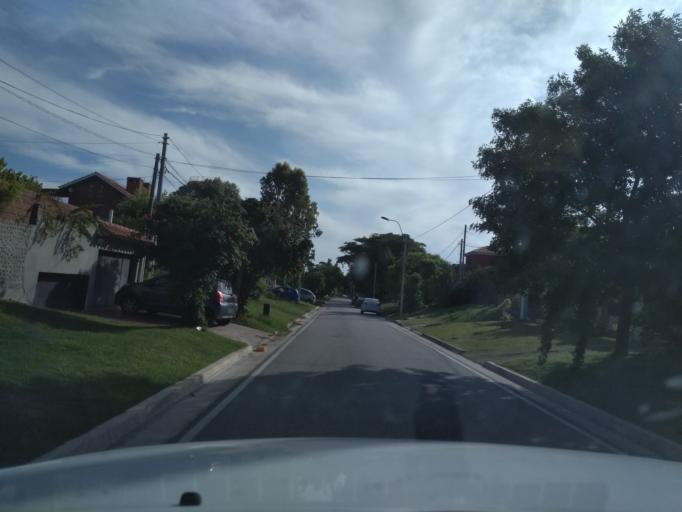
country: UY
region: Canelones
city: Barra de Carrasco
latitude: -34.8684
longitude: -56.0350
